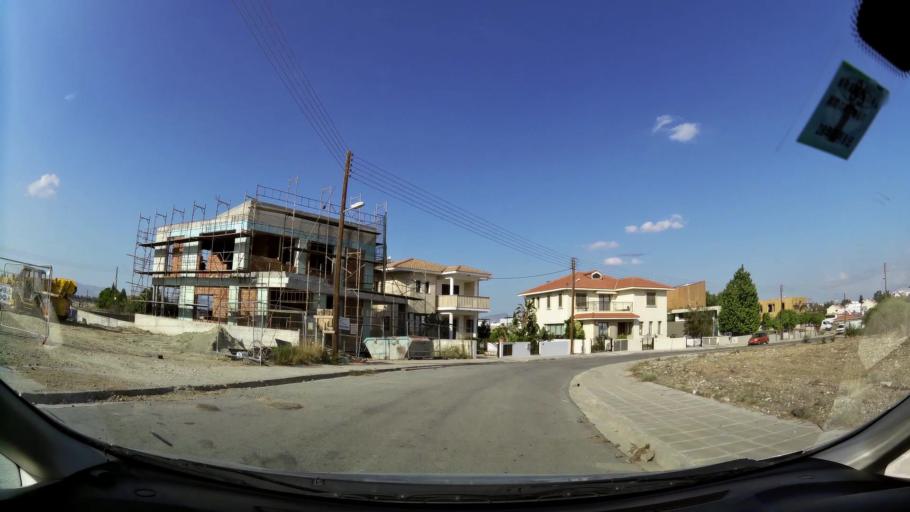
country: CY
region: Lefkosia
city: Kato Deftera
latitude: 35.1392
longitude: 33.2974
